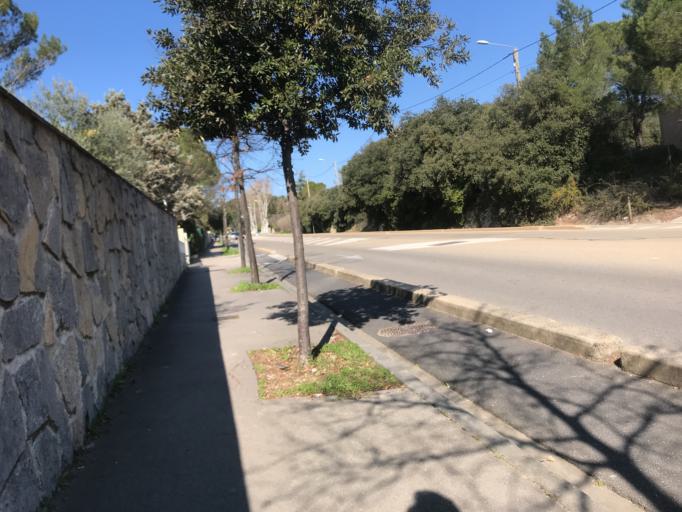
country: FR
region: Languedoc-Roussillon
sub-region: Departement de l'Herault
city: Montferrier-sur-Lez
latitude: 43.6392
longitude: 3.8650
